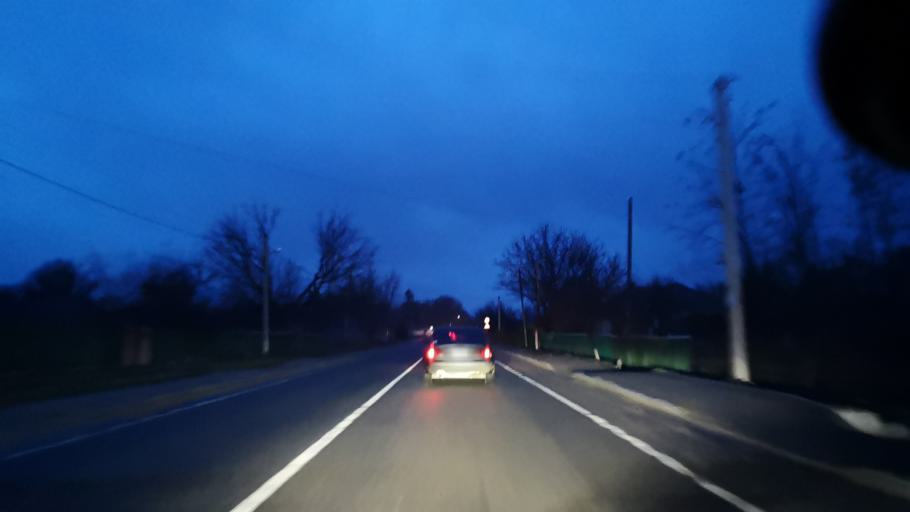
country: MD
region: Orhei
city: Orhei
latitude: 47.4363
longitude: 28.7975
